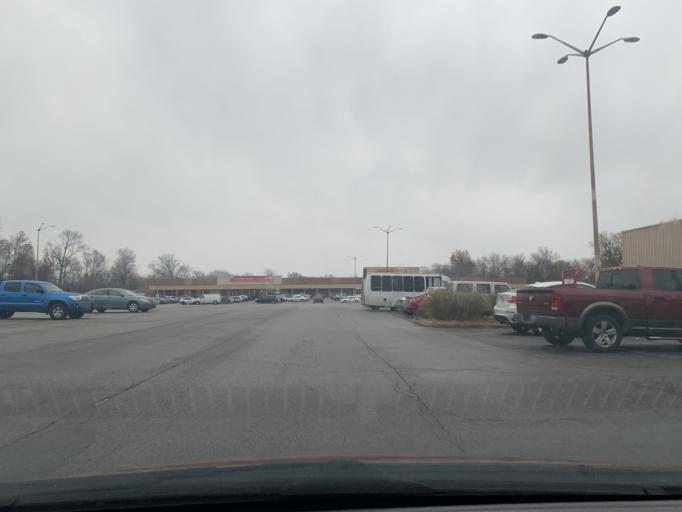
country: US
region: Kentucky
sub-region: Jefferson County
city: Okolona
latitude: 38.1609
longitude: -85.6986
